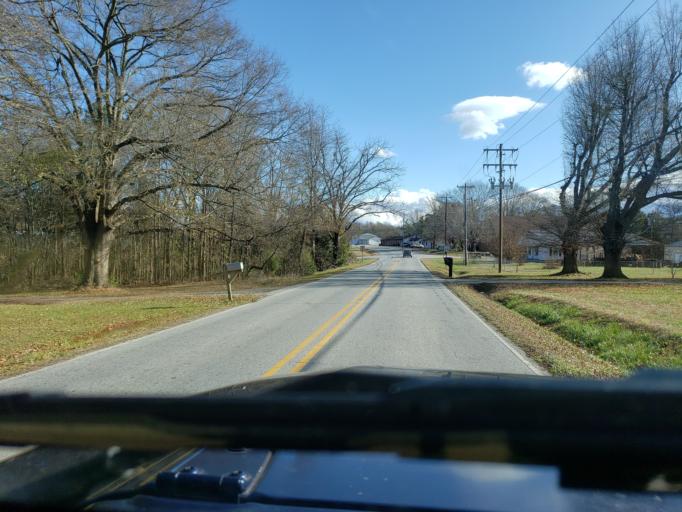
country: US
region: North Carolina
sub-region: Cleveland County
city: White Plains
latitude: 35.1785
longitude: -81.4569
